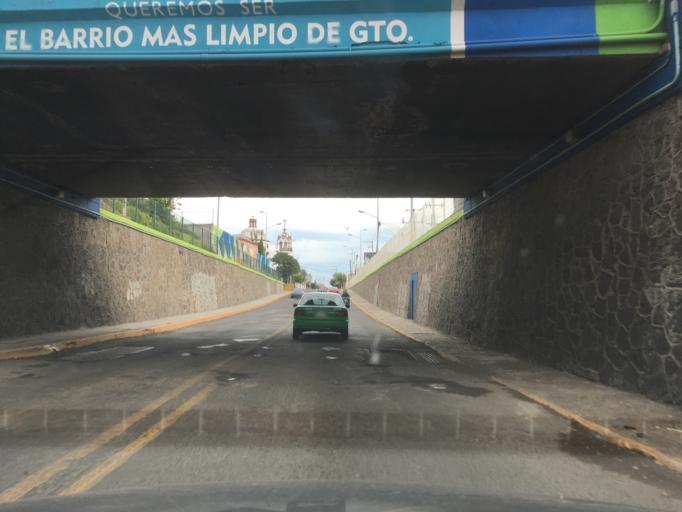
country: MX
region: Guanajuato
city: Celaya
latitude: 20.5322
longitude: -100.8189
